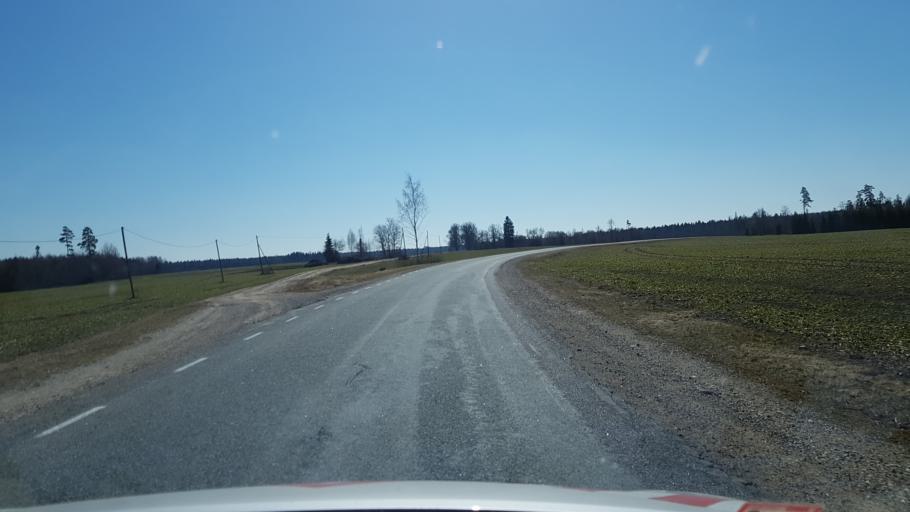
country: EE
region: Laeaene-Virumaa
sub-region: Rakke vald
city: Rakke
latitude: 59.0234
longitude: 26.3530
